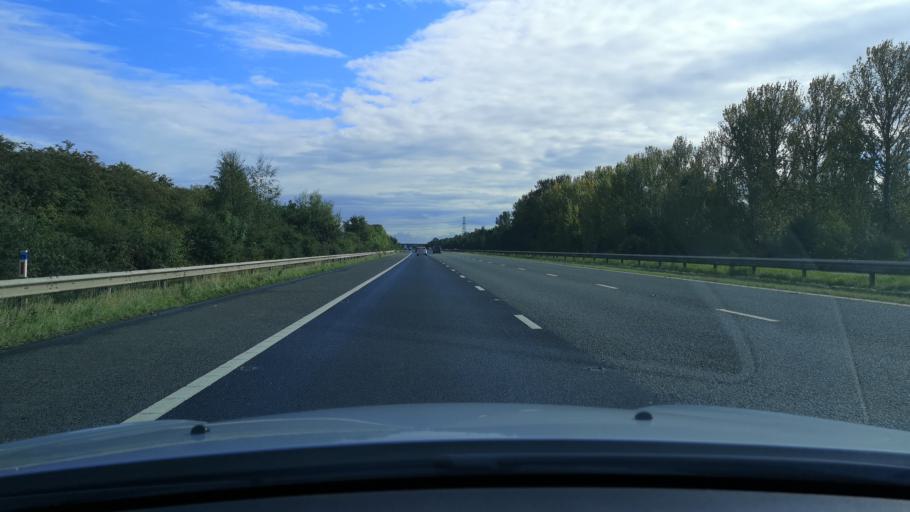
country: GB
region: England
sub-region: East Riding of Yorkshire
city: Pollington
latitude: 53.6823
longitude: -1.0685
